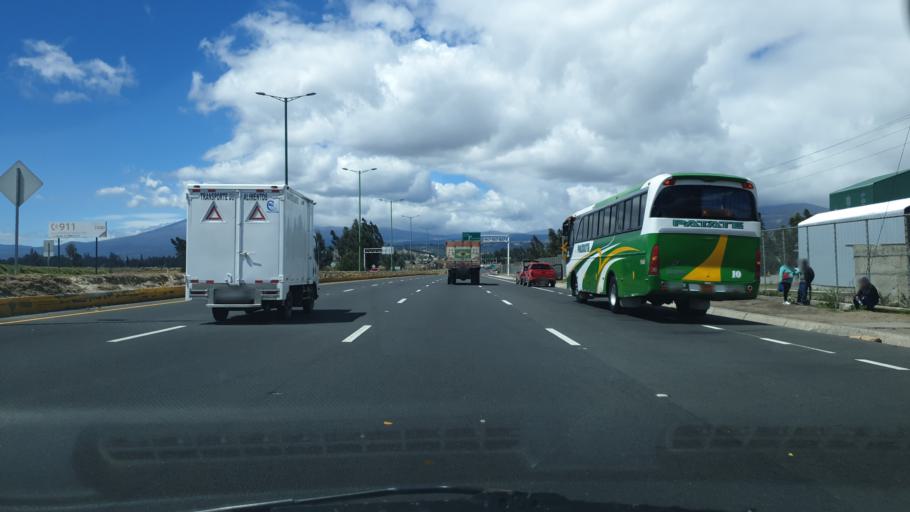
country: EC
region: Cotopaxi
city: Saquisili
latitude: -0.8710
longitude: -78.6372
